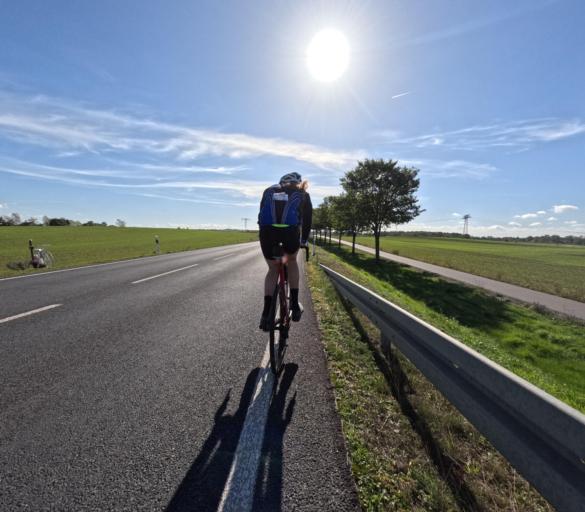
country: DE
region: Saxony
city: Moritzburg
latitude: 51.1419
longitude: 13.6517
